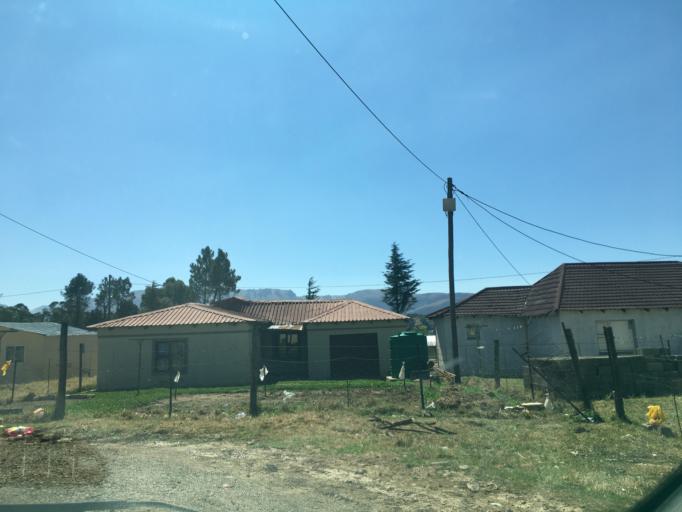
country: ZA
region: Eastern Cape
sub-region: Chris Hani District Municipality
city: Elliot
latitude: -31.3381
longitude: 27.8363
